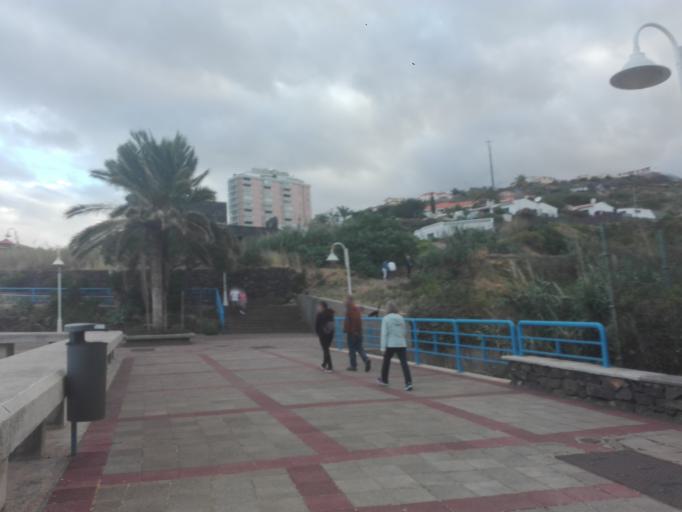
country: PT
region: Madeira
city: Canico
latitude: 32.6450
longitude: -16.8272
